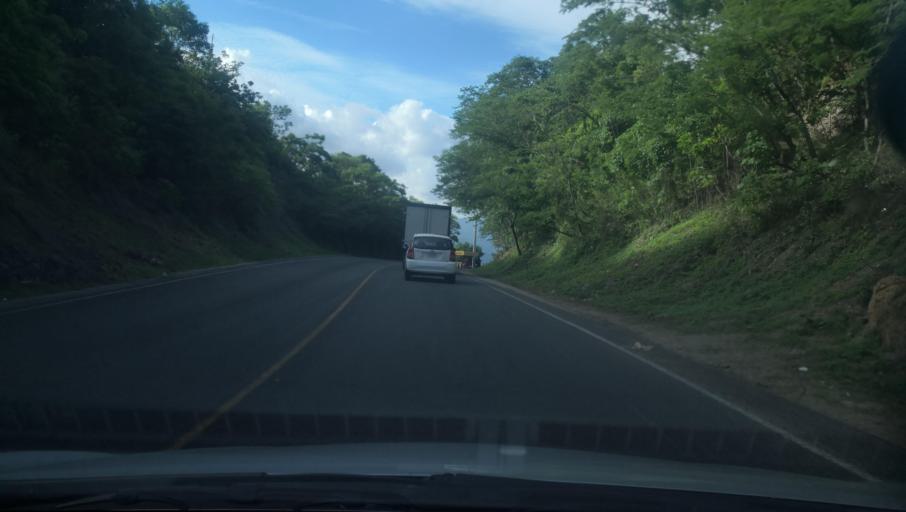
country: NI
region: Madriz
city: Totogalpa
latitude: 13.5867
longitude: -86.4739
